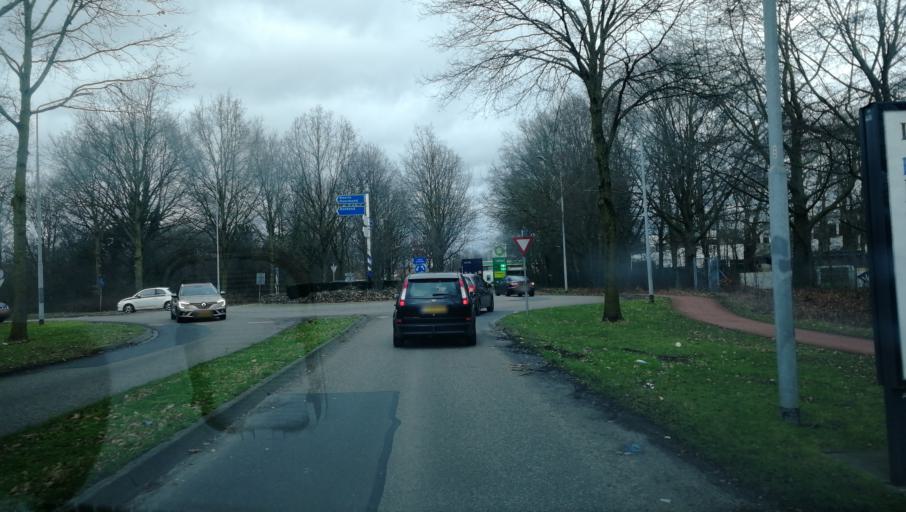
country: NL
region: Limburg
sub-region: Gemeente Venlo
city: Tegelen
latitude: 51.3711
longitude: 6.1360
